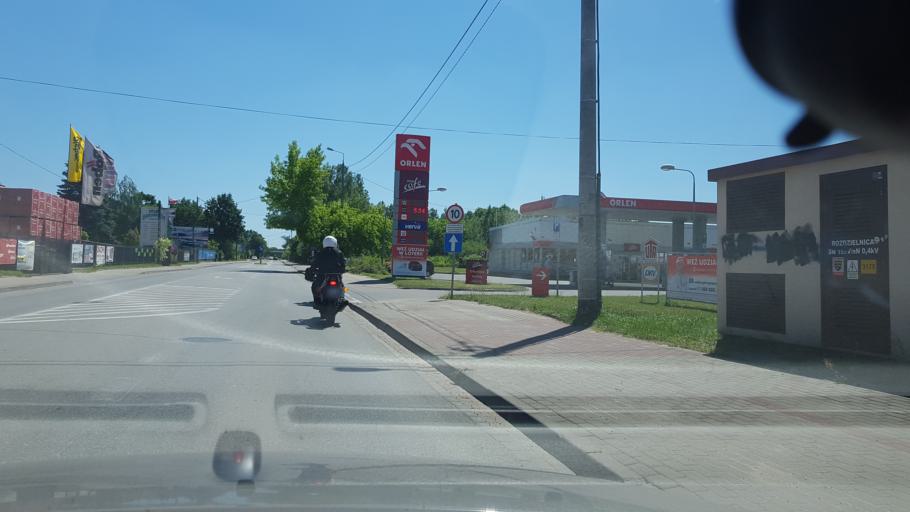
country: PL
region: Masovian Voivodeship
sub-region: Powiat wolominski
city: Marki
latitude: 52.3164
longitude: 21.1176
